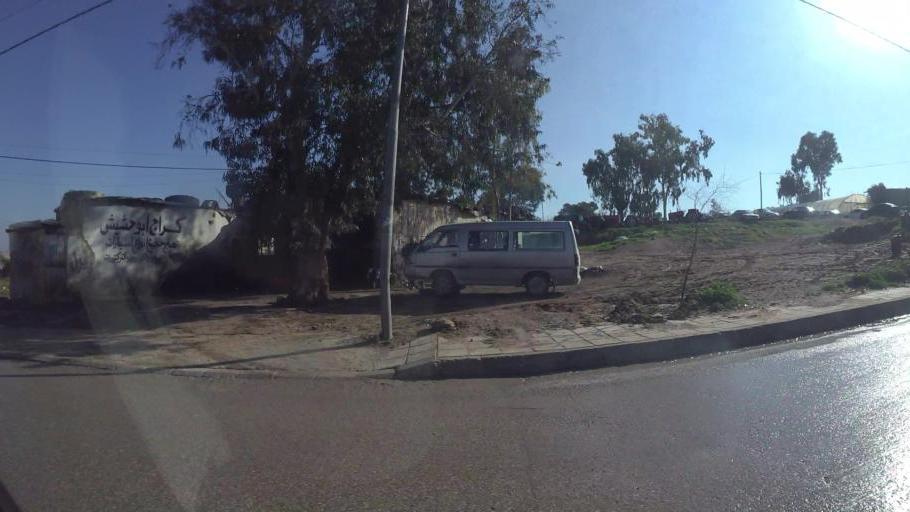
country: JO
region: Amman
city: Al Jubayhah
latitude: 32.0622
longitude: 35.8402
